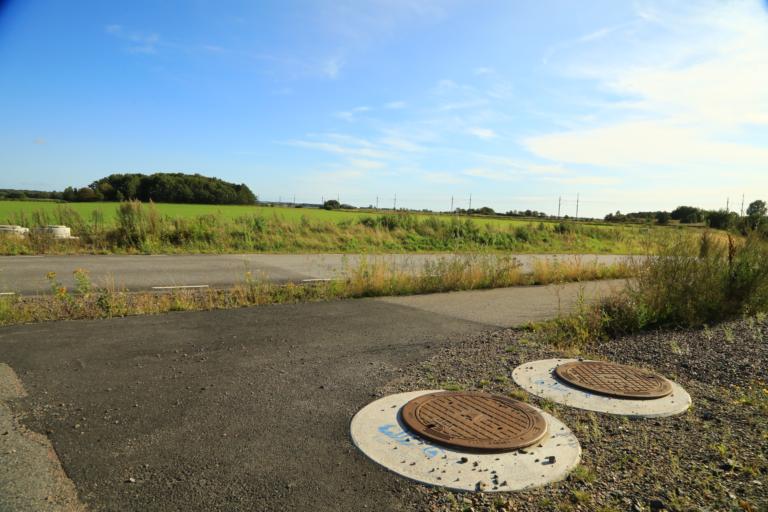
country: SE
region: Halland
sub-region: Varbergs Kommun
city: Varberg
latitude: 57.1503
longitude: 12.2539
